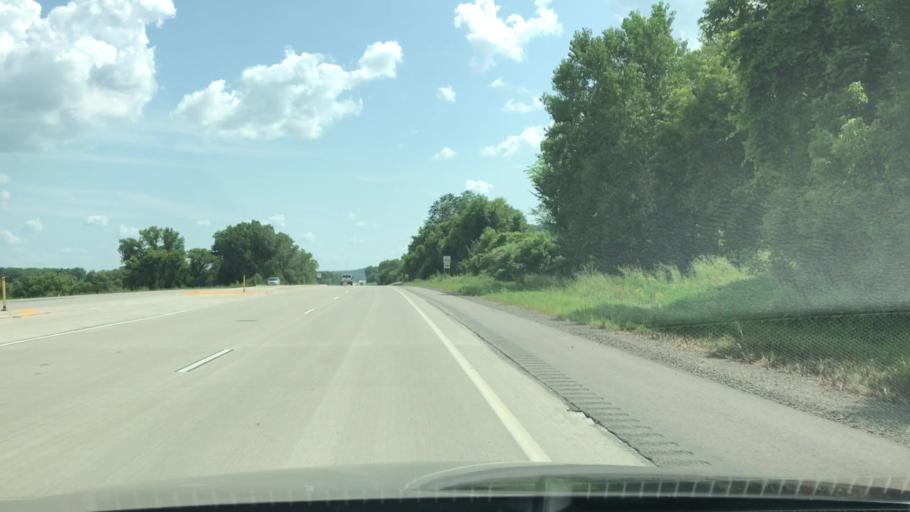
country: US
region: Minnesota
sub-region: Nicollet County
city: North Mankato
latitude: 44.2564
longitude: -94.0277
